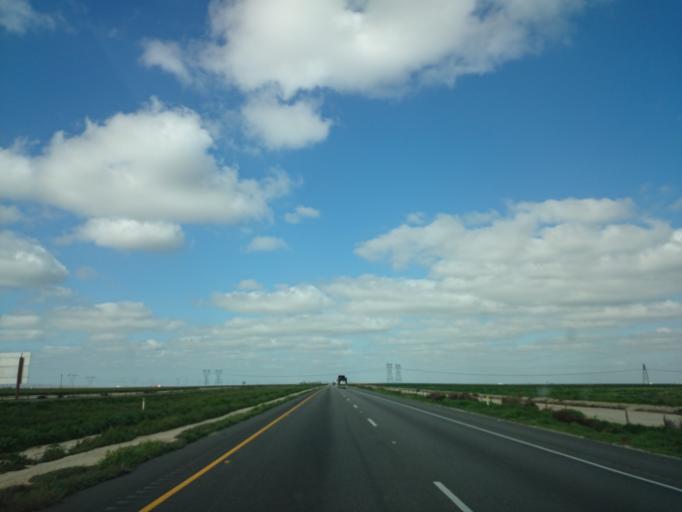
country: US
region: California
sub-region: Kern County
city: Rosedale
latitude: 35.2216
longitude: -119.1760
